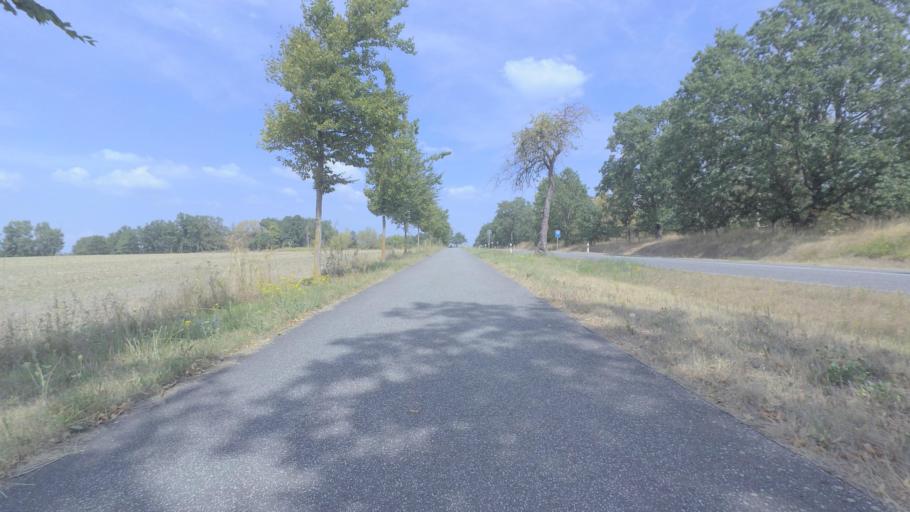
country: DE
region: Brandenburg
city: Wustermark
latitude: 52.5301
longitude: 12.9770
